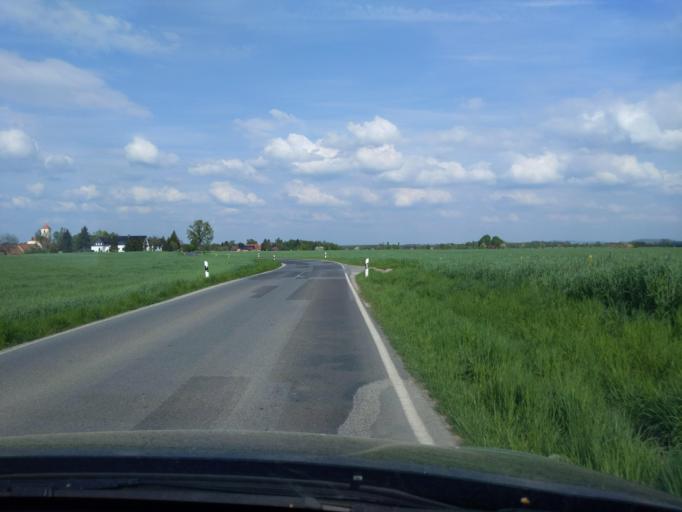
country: DE
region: Saxony
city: Malschwitz
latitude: 51.1992
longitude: 14.5165
